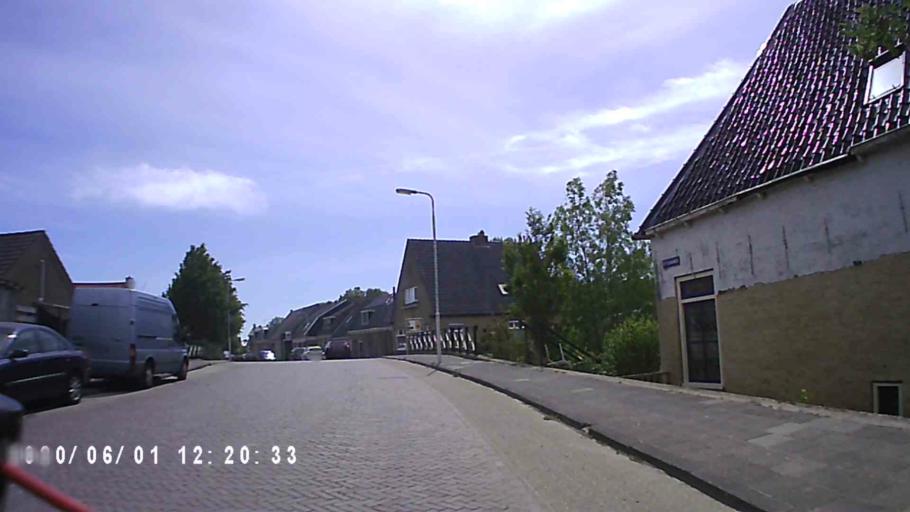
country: NL
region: Friesland
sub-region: Gemeente Harlingen
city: Harlingen
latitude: 53.1296
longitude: 5.4769
